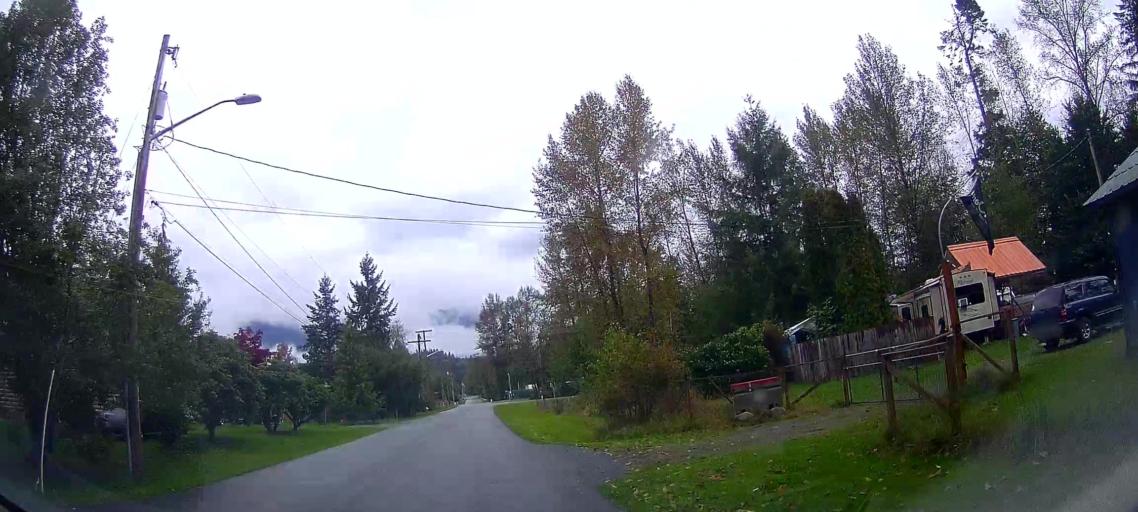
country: US
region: Washington
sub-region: Skagit County
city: Sedro-Woolley
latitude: 48.5243
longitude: -121.9902
